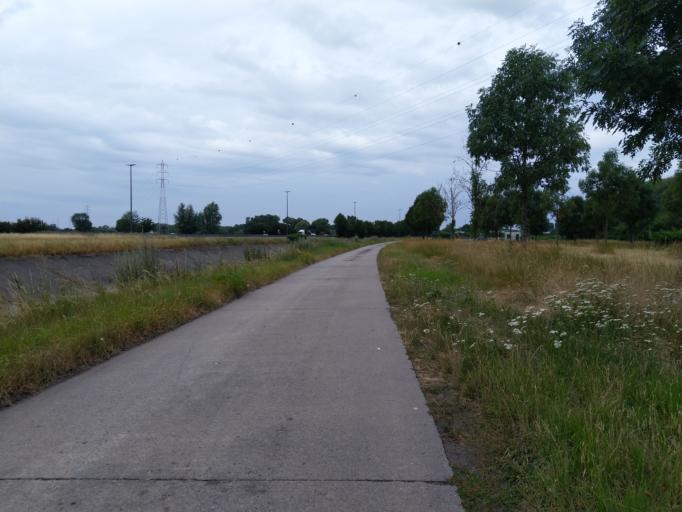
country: BE
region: Wallonia
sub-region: Province du Hainaut
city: Boussu
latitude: 50.4529
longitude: 3.7984
